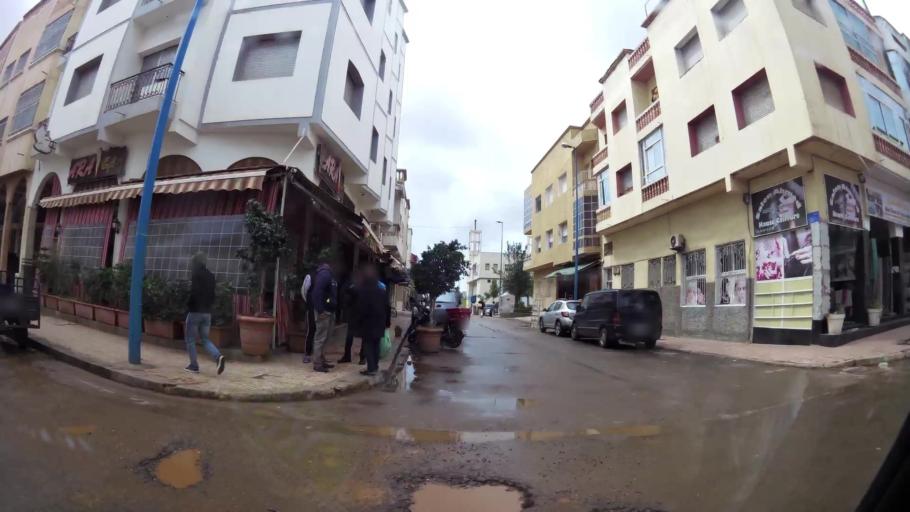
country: MA
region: Grand Casablanca
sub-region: Casablanca
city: Casablanca
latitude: 33.5342
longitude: -7.6511
